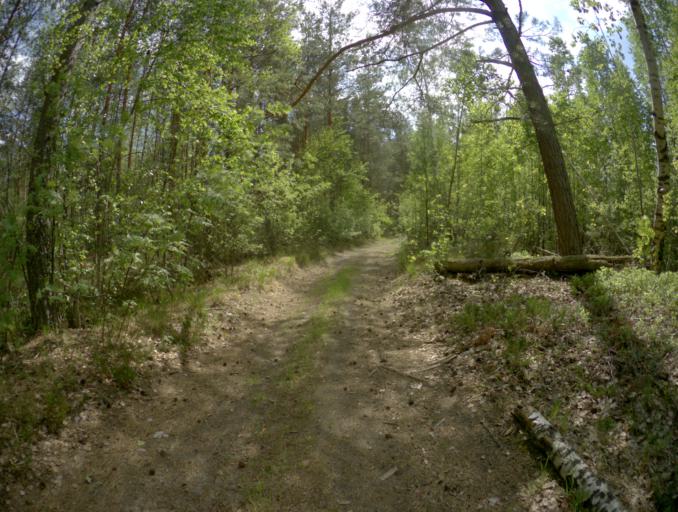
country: RU
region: Vladimir
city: Ivanishchi
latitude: 55.6854
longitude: 40.4007
